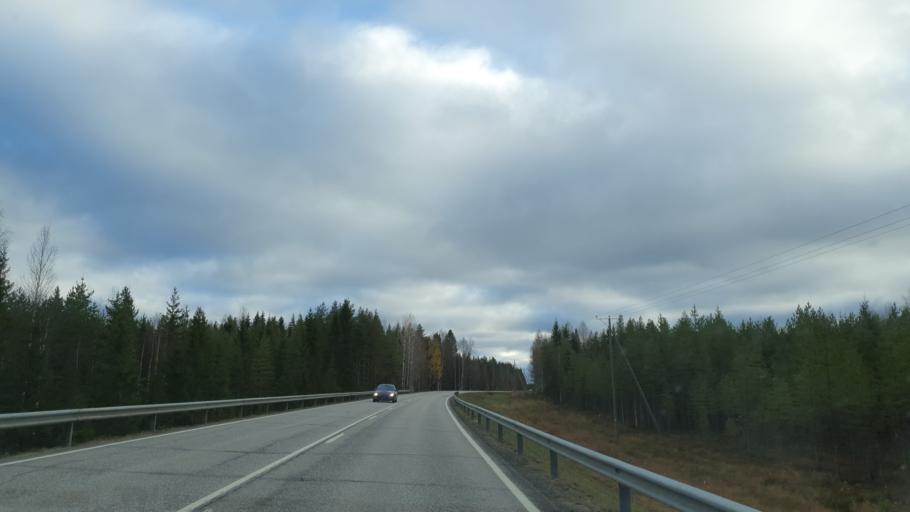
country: FI
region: Kainuu
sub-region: Kajaani
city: Sotkamo
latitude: 64.0917
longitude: 28.7974
